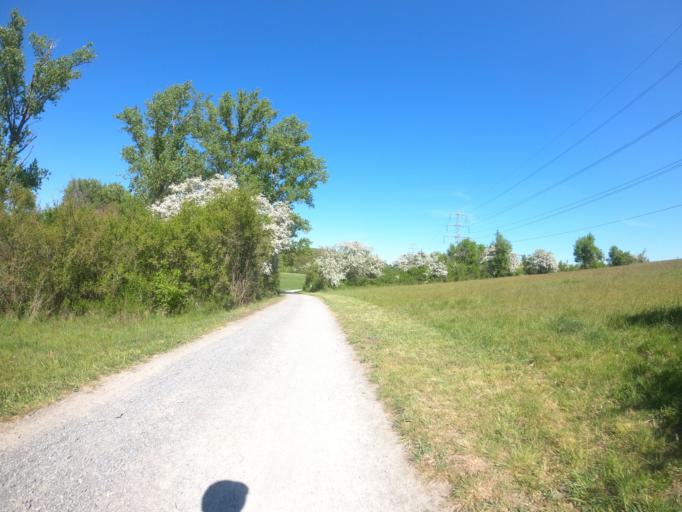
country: DE
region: Hesse
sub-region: Regierungsbezirk Darmstadt
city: Florsheim
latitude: 50.0146
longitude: 8.3973
